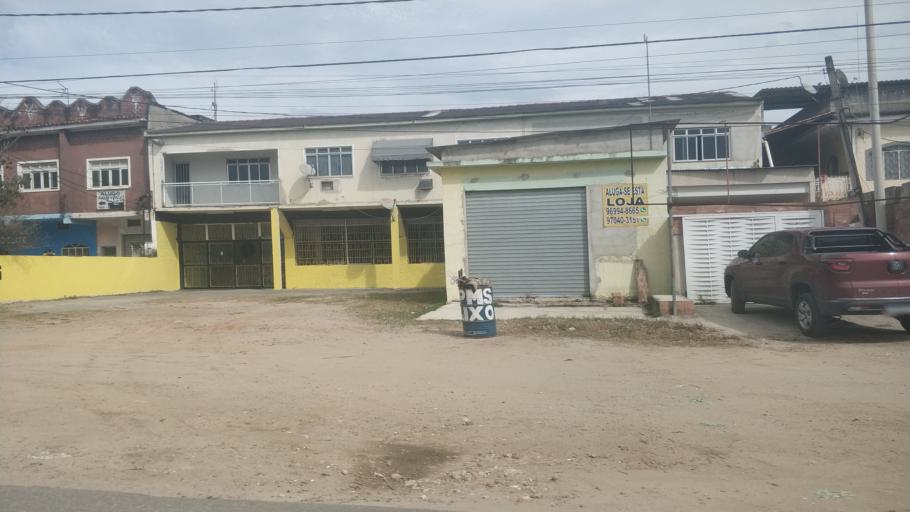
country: BR
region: Rio de Janeiro
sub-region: Seropedica
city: Seropedica
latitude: -22.8084
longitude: -43.6343
